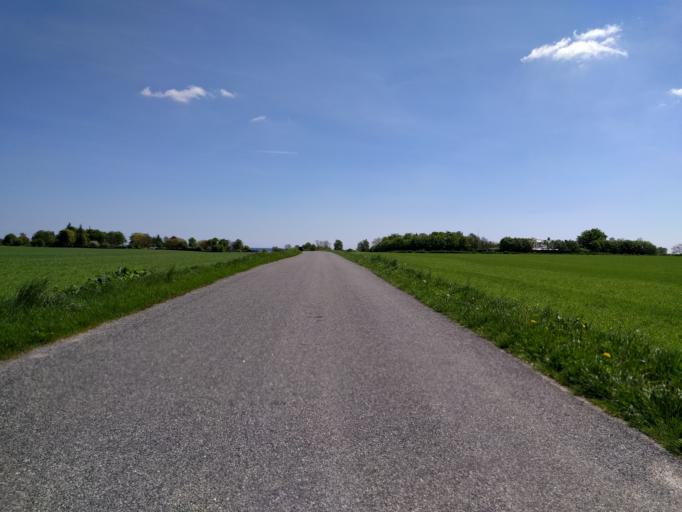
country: DK
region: Zealand
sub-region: Guldborgsund Kommune
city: Stubbekobing
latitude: 54.7450
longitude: 12.0238
